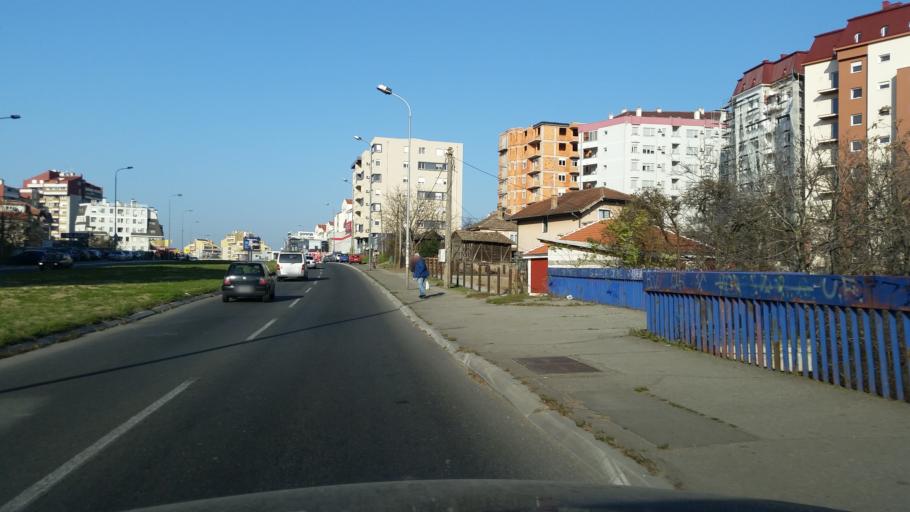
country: RS
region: Central Serbia
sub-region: Belgrade
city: Cukarica
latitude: 44.7567
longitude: 20.4154
